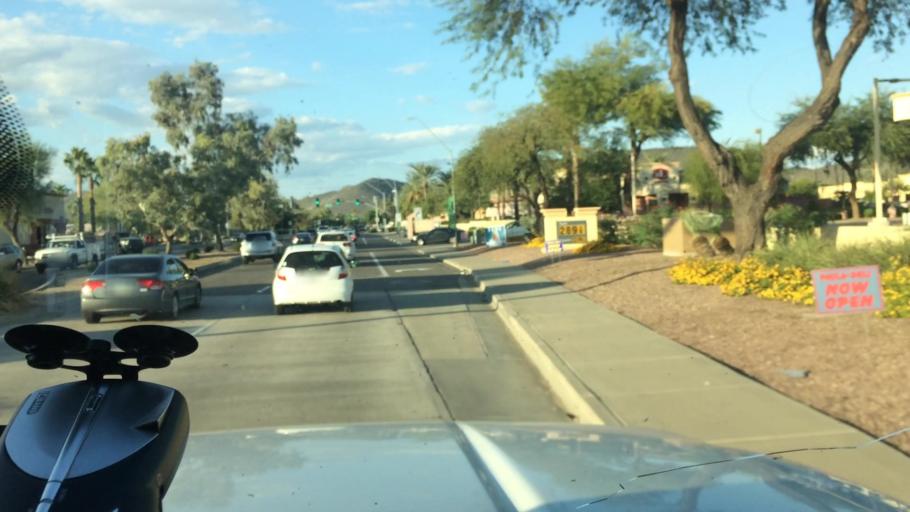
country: US
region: Arizona
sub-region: Maricopa County
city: Peoria
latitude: 33.6691
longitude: -112.1866
